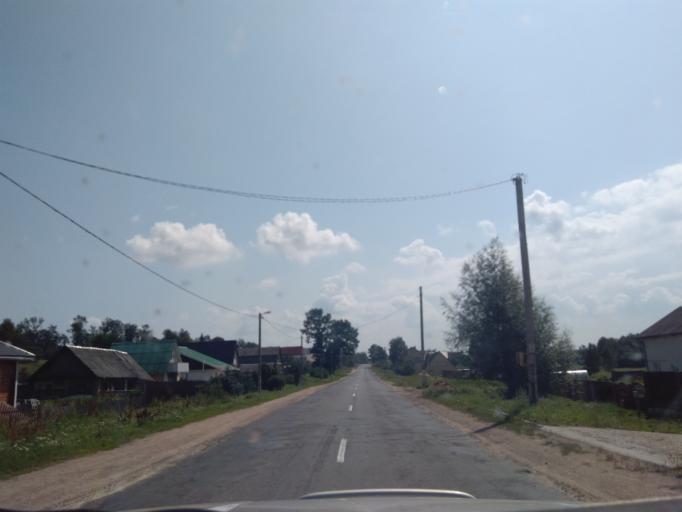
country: BY
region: Minsk
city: Khatsyezhyna
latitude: 53.8924
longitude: 27.2577
